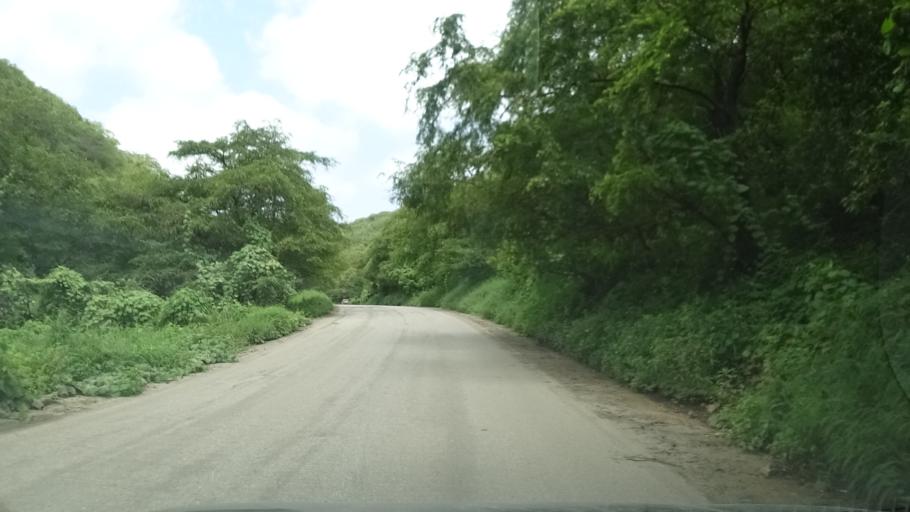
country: OM
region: Zufar
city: Salalah
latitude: 17.1732
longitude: 54.1663
